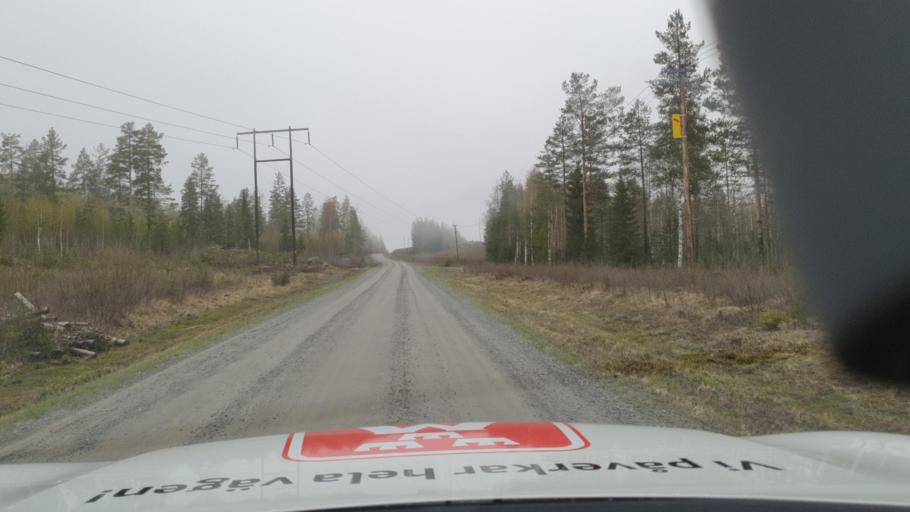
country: SE
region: Vaesterbotten
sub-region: Nordmalings Kommun
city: Nordmaling
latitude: 63.7479
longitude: 19.4999
